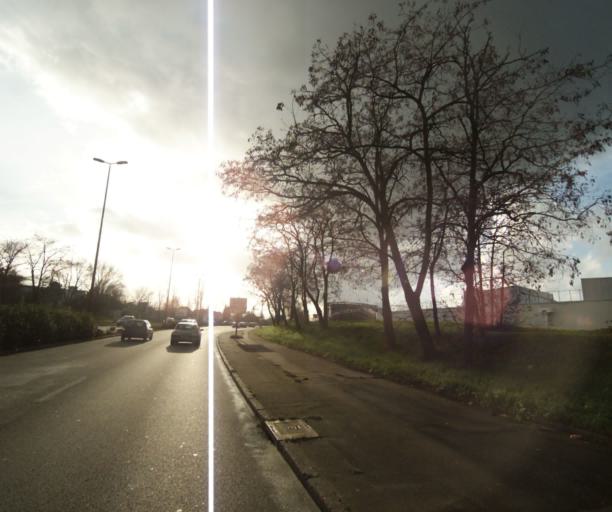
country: FR
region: Pays de la Loire
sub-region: Departement de la Sarthe
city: Le Mans
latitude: 47.9872
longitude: 0.2264
